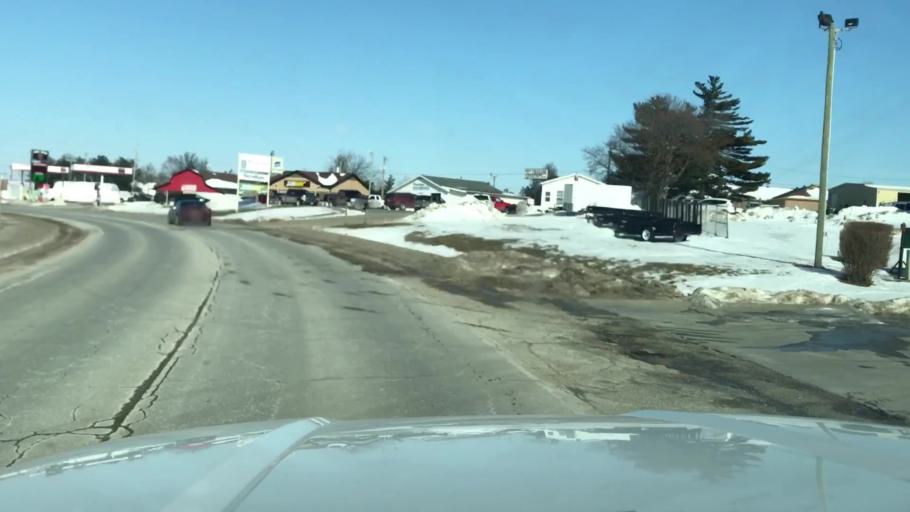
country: US
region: Missouri
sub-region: Andrew County
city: Savannah
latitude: 39.9456
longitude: -94.8219
